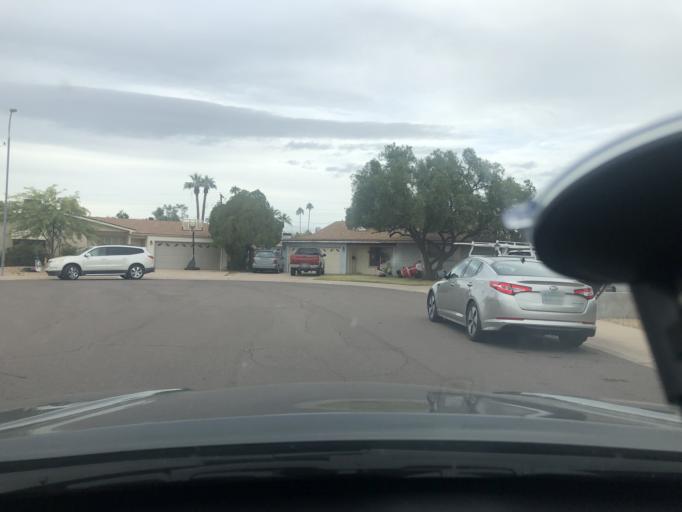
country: US
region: Arizona
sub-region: Maricopa County
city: Scottsdale
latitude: 33.4933
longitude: -111.8968
